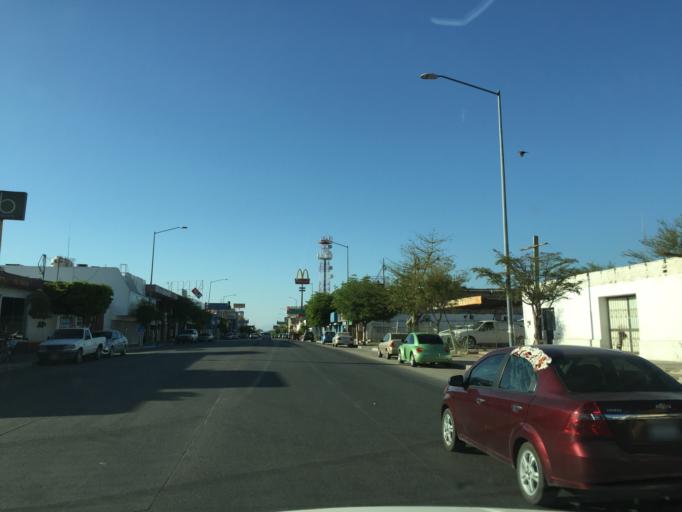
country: MX
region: Sonora
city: Navojoa
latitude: 27.0771
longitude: -109.4443
